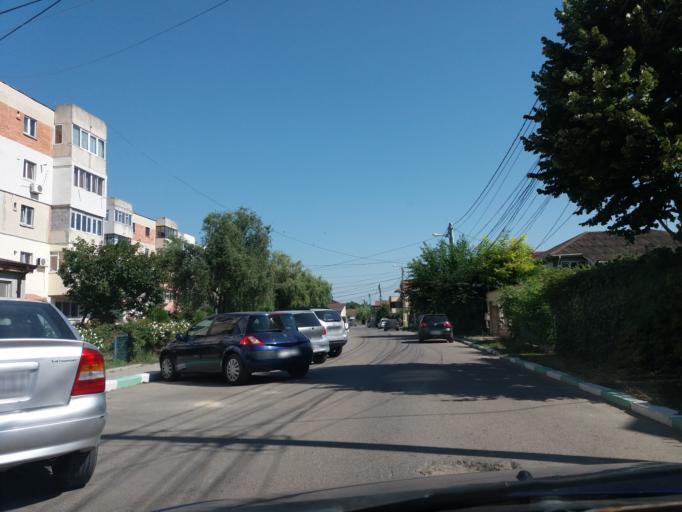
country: RO
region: Constanta
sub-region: Comuna Navodari
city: Navodari
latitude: 44.3250
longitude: 28.6118
